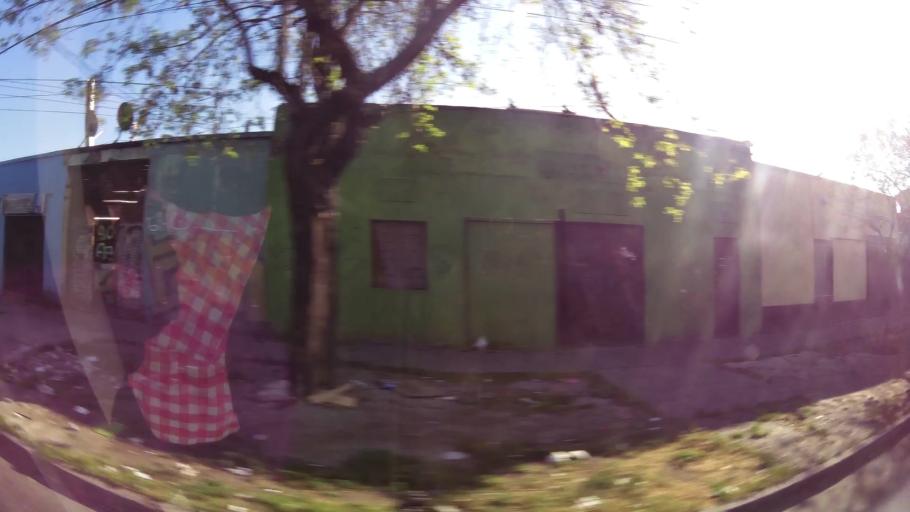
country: CL
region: Santiago Metropolitan
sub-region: Provincia de Santiago
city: Santiago
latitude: -33.4877
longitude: -70.6421
